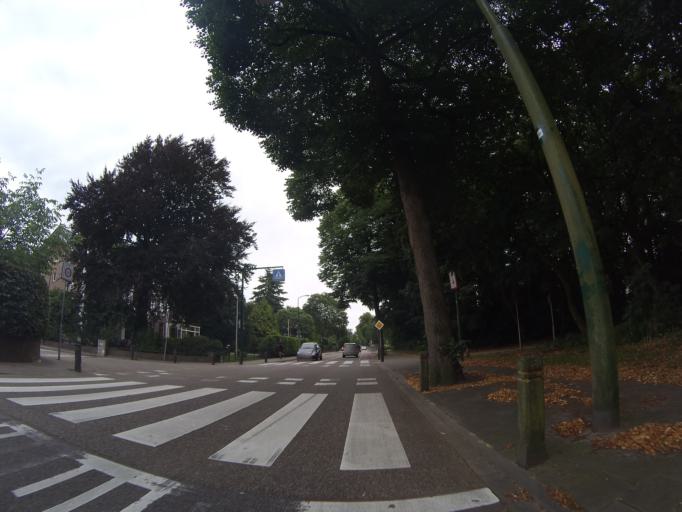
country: NL
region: Utrecht
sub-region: Gemeente Baarn
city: Baarn
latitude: 52.2152
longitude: 5.2801
